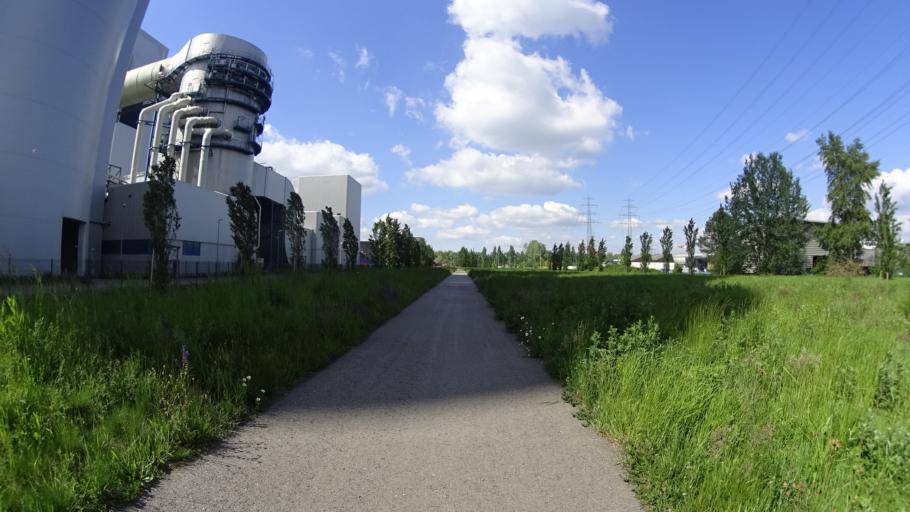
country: DE
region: Baden-Wuerttemberg
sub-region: Karlsruhe Region
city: Rheinstetten
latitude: 49.0123
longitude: 8.3098
